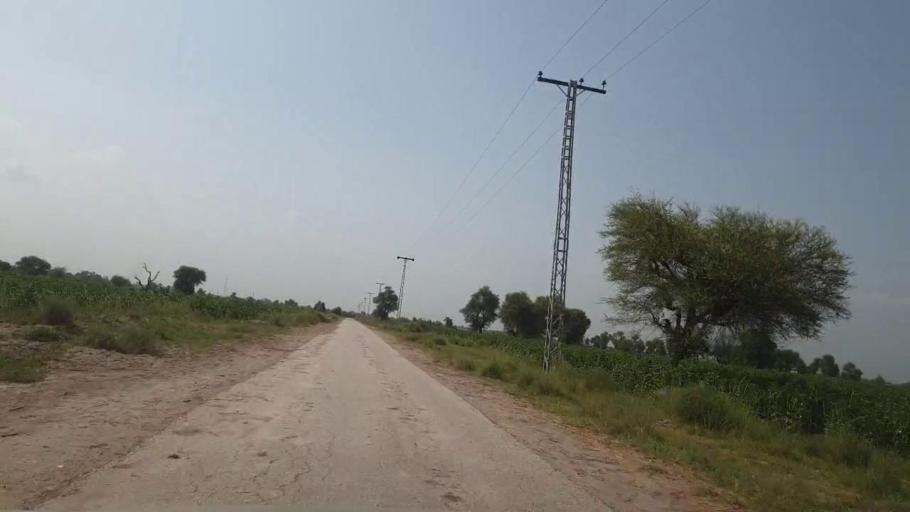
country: PK
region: Sindh
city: Pano Aqil
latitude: 27.7867
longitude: 69.1567
